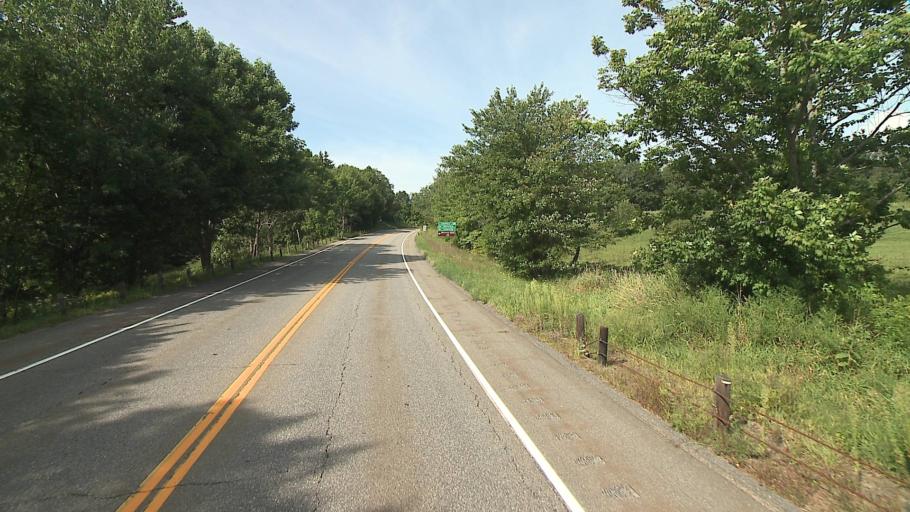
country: US
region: Connecticut
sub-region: Litchfield County
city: Litchfield
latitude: 41.7445
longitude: -73.1670
